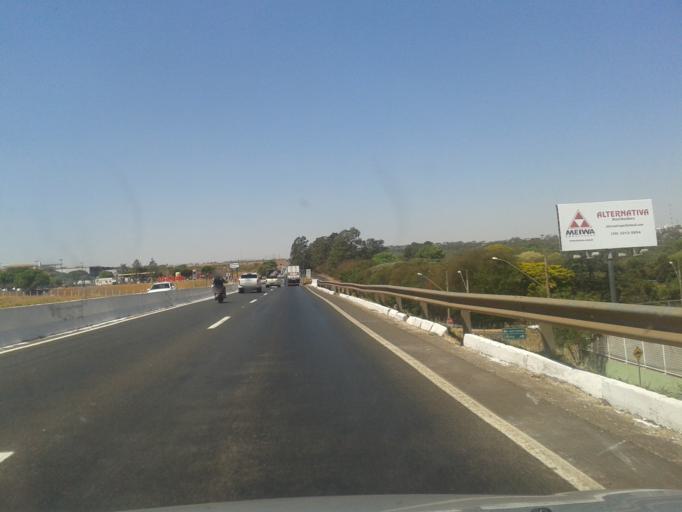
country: BR
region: Minas Gerais
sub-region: Uberlandia
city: Uberlandia
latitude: -18.9025
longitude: -48.2363
